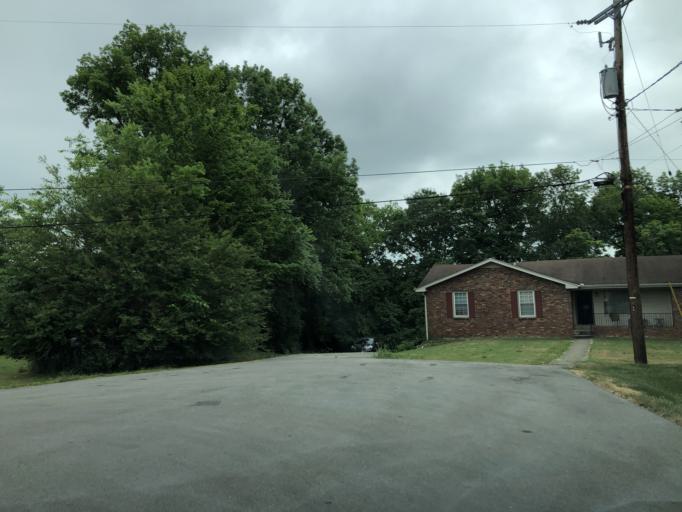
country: US
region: Tennessee
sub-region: Davidson County
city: Goodlettsville
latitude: 36.2800
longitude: -86.7693
